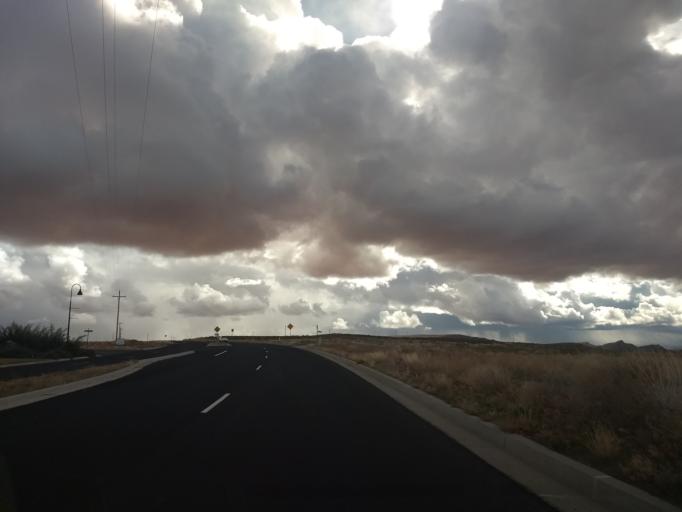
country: US
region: Utah
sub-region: Washington County
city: Hurricane
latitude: 37.1486
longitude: -113.3896
